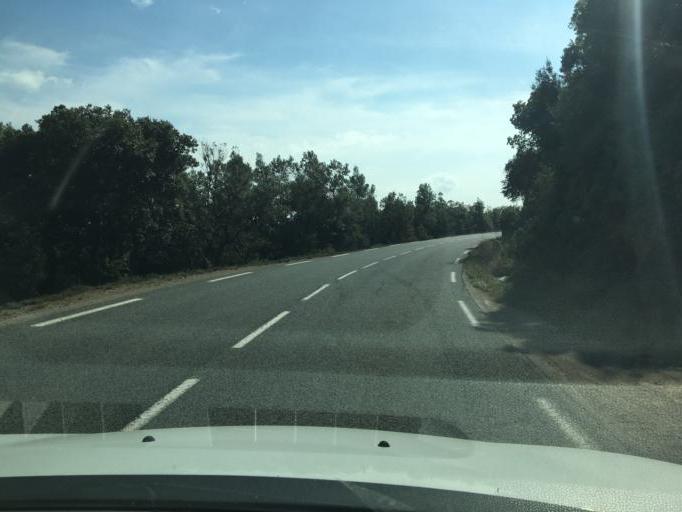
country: FR
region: Provence-Alpes-Cote d'Azur
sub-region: Departement du Var
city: Bargemon
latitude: 43.6100
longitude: 6.5517
